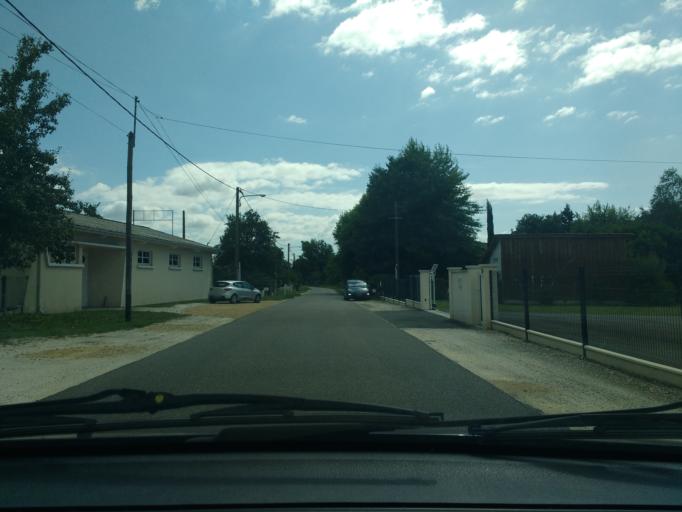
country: FR
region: Aquitaine
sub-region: Departement de la Gironde
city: Salles
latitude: 44.5590
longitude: -0.8556
